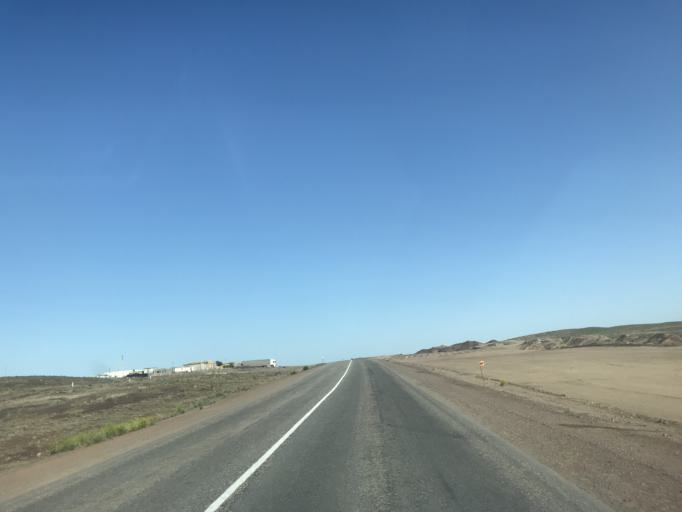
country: KZ
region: Zhambyl
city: Mynaral
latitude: 45.3283
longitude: 73.7302
